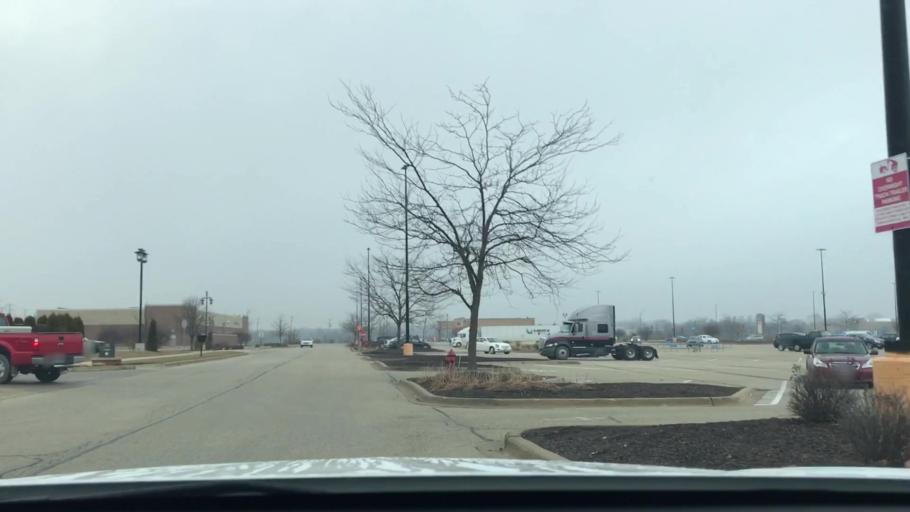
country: US
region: Illinois
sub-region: McHenry County
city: Huntley
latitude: 42.1510
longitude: -88.4313
